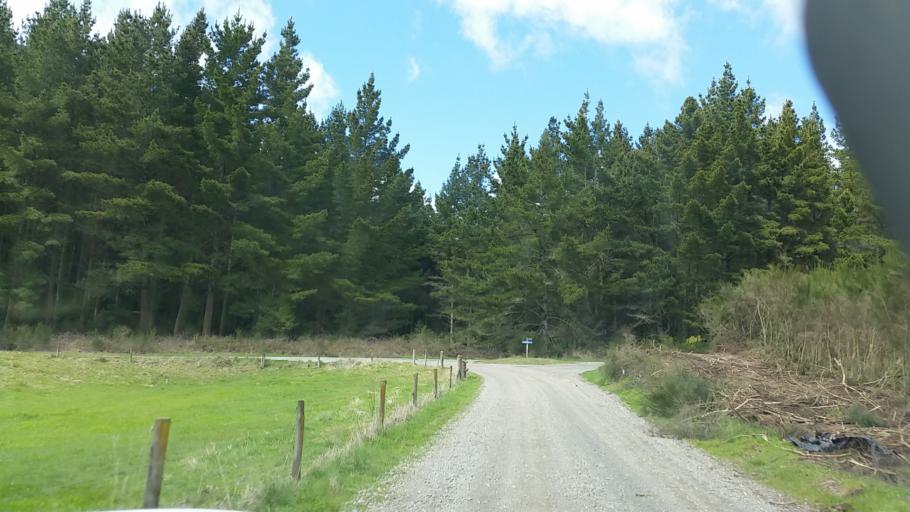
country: NZ
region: Bay of Plenty
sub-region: Whakatane District
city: Murupara
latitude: -38.3454
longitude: 176.5441
